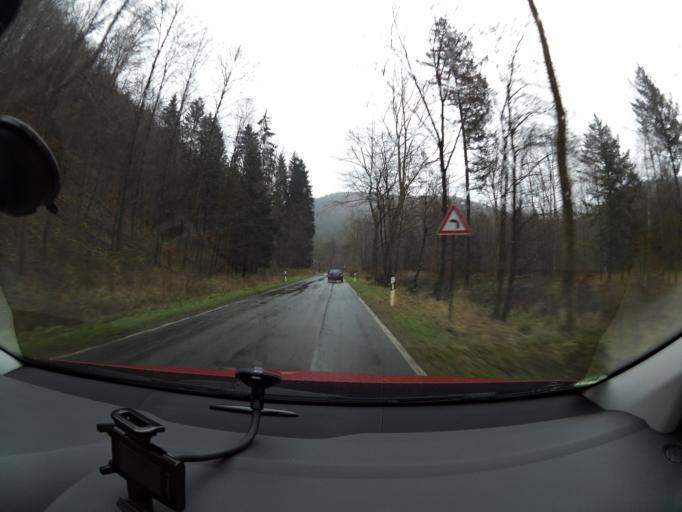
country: DE
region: Lower Saxony
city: Herzberg am Harz
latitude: 51.6808
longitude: 10.3957
